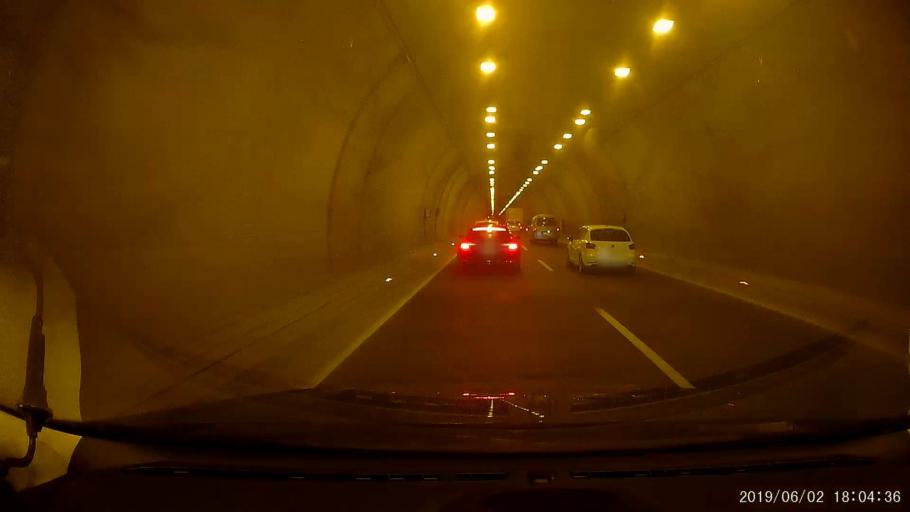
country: TR
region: Ordu
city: Unieh
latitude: 41.1195
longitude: 37.2324
